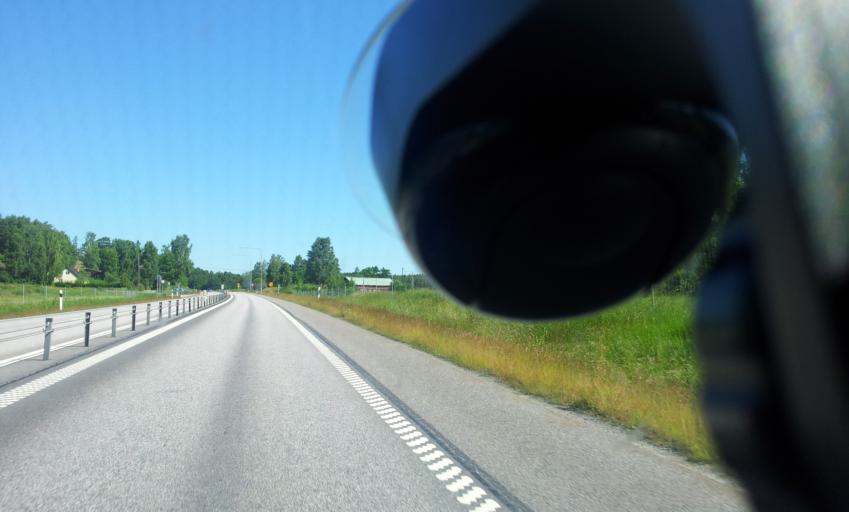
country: SE
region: OEstergoetland
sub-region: Soderkopings Kommun
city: Soederkoeping
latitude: 58.4074
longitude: 16.4019
